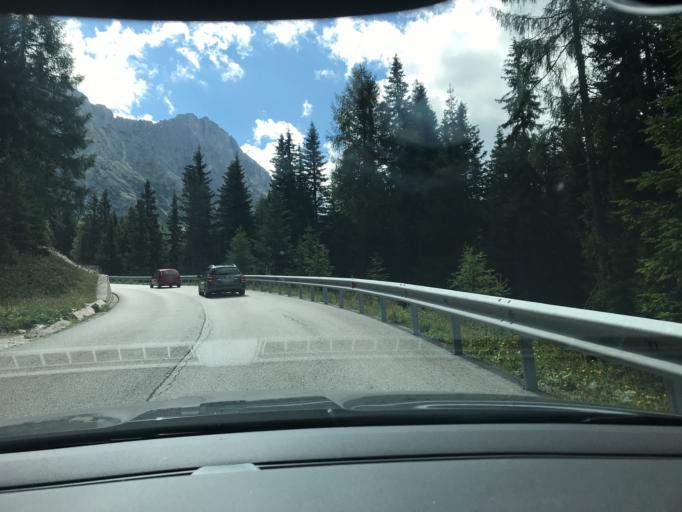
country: IT
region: Veneto
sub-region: Provincia di Belluno
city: Livinallongo del Col di Lana
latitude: 46.5430
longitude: 11.9743
